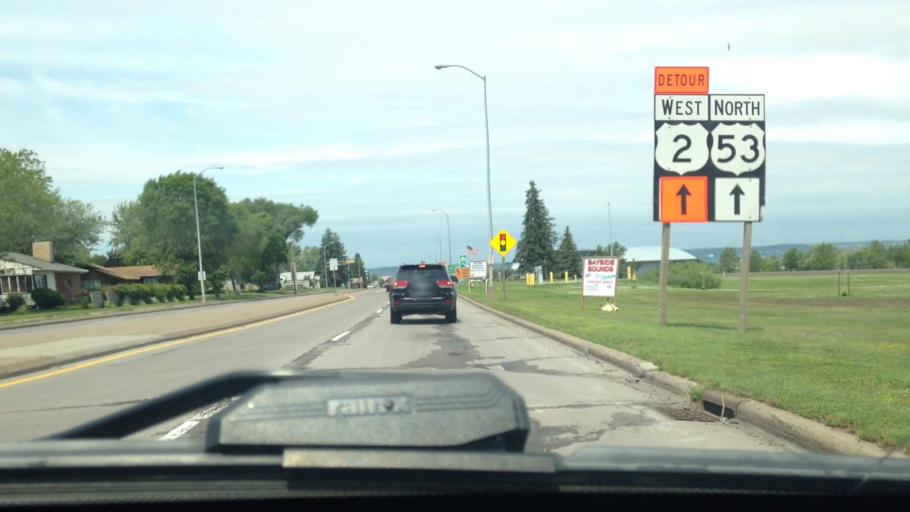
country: US
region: Wisconsin
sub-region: Douglas County
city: Superior
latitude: 46.7210
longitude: -92.0663
